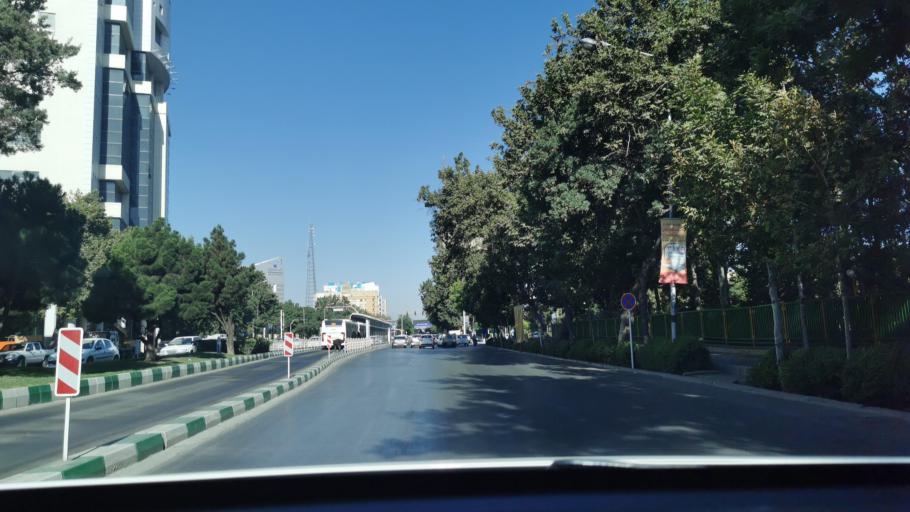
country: IR
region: Razavi Khorasan
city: Mashhad
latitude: 36.3241
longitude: 59.5717
